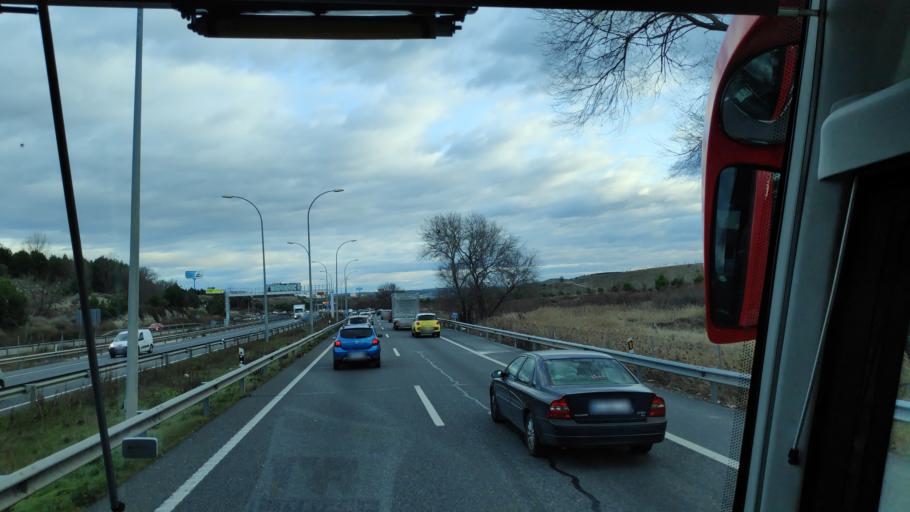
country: ES
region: Madrid
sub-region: Provincia de Madrid
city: Vaciamadrid
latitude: 40.3491
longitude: -3.5472
